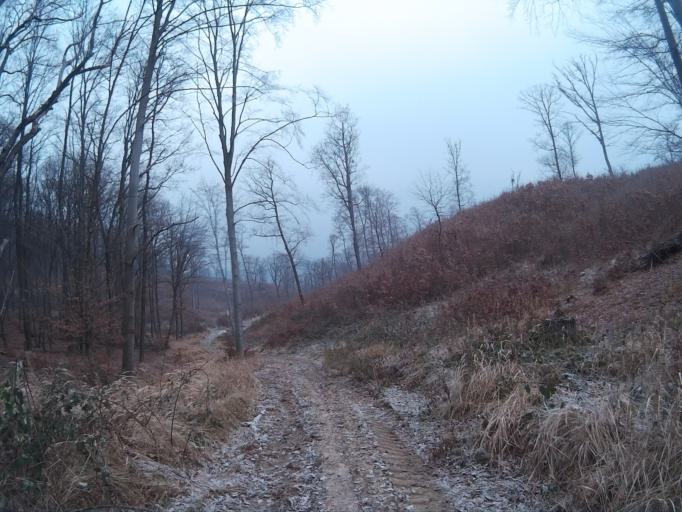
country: HU
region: Nograd
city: Rimoc
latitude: 47.9827
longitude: 19.5693
